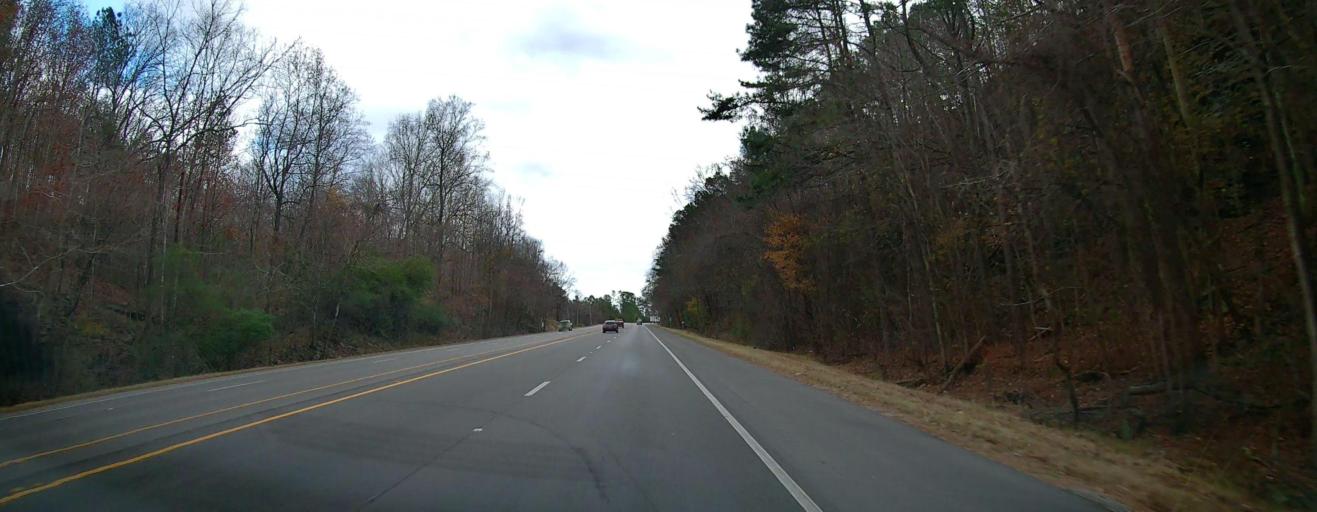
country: US
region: Alabama
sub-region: Morgan County
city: Falkville
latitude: 34.3100
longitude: -86.9978
